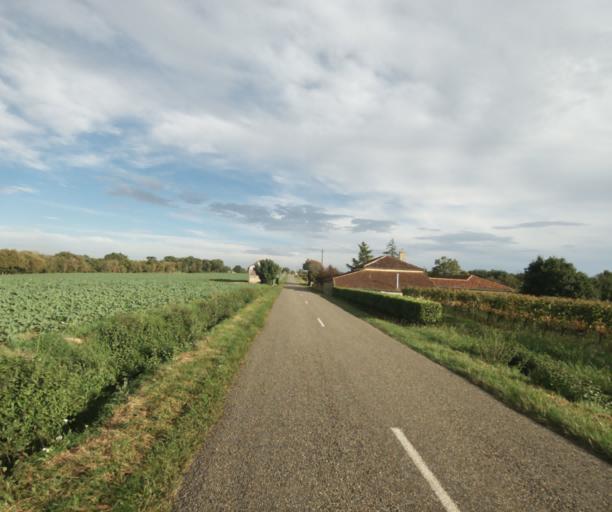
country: FR
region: Midi-Pyrenees
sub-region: Departement du Gers
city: Le Houga
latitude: 43.8601
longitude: -0.1501
